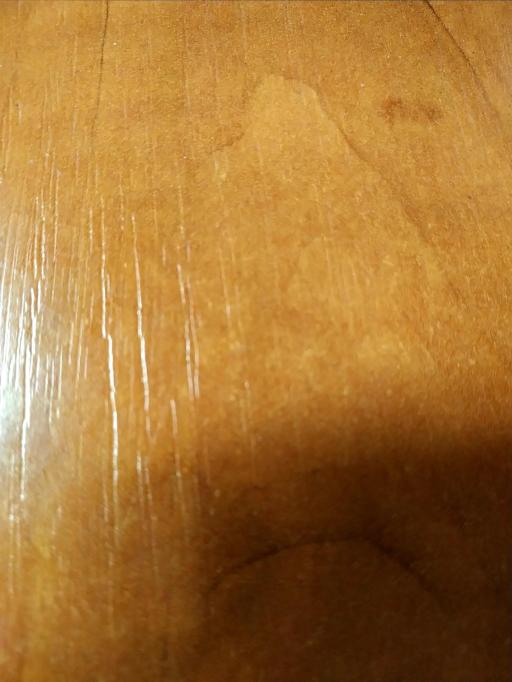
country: RU
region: Smolensk
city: Yartsevo
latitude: 55.4312
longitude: 32.8147
